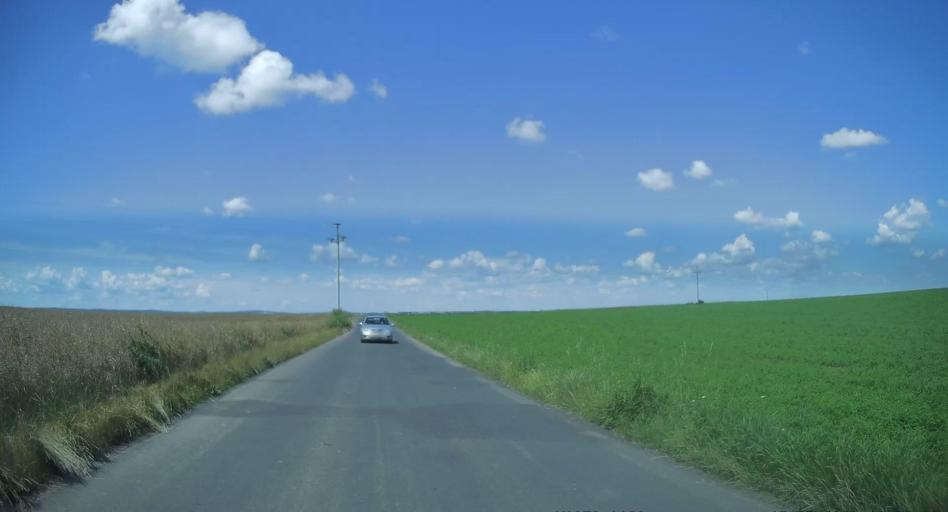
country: PL
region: Subcarpathian Voivodeship
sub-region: Powiat jaroslawski
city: Sosnica
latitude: 49.8491
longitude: 22.8827
